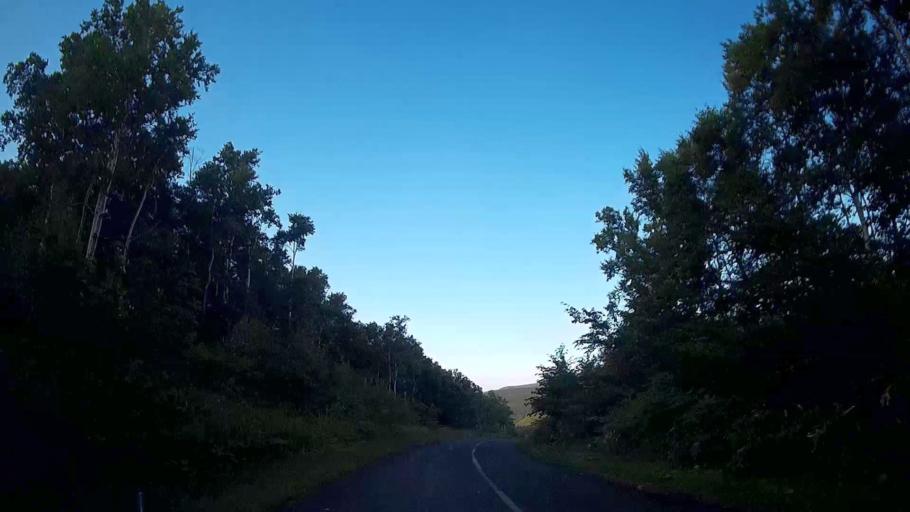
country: JP
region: Hokkaido
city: Iwanai
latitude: 42.6336
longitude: 140.0295
